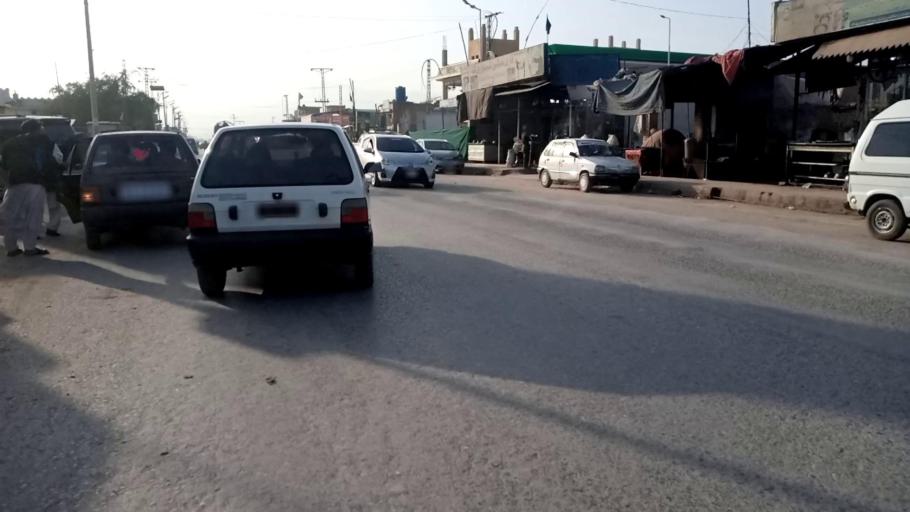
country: PK
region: Khyber Pakhtunkhwa
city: Peshawar
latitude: 33.9985
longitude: 71.4205
